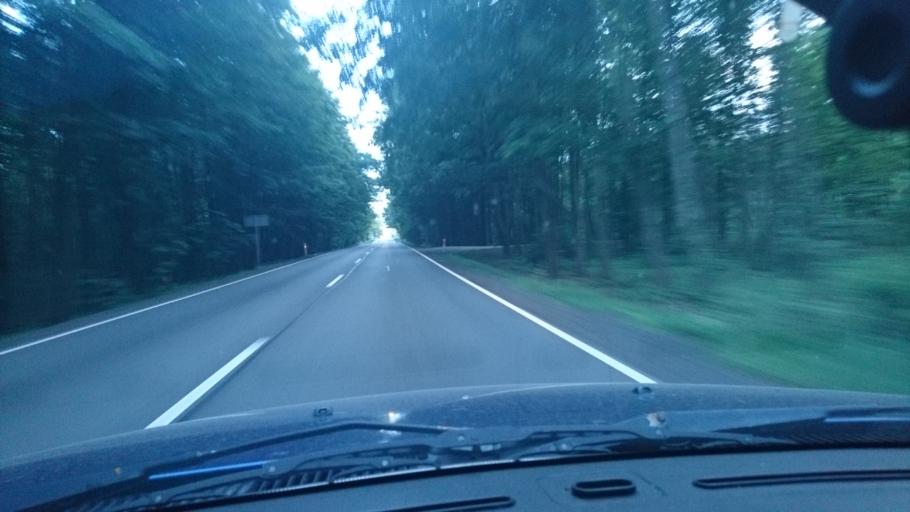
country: PL
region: Silesian Voivodeship
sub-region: Powiat tarnogorski
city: Wieszowa
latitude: 50.4069
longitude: 18.8144
